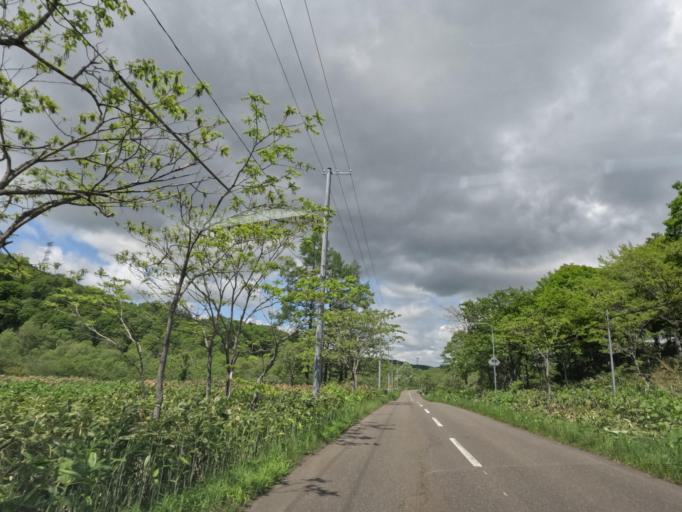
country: JP
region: Hokkaido
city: Tobetsu
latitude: 43.4459
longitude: 141.5838
